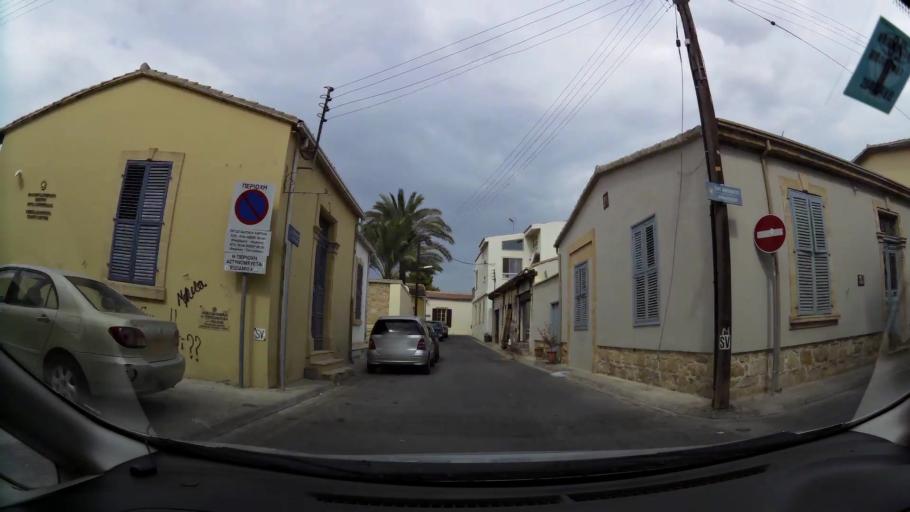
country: CY
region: Lefkosia
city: Nicosia
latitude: 35.1757
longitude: 33.3702
